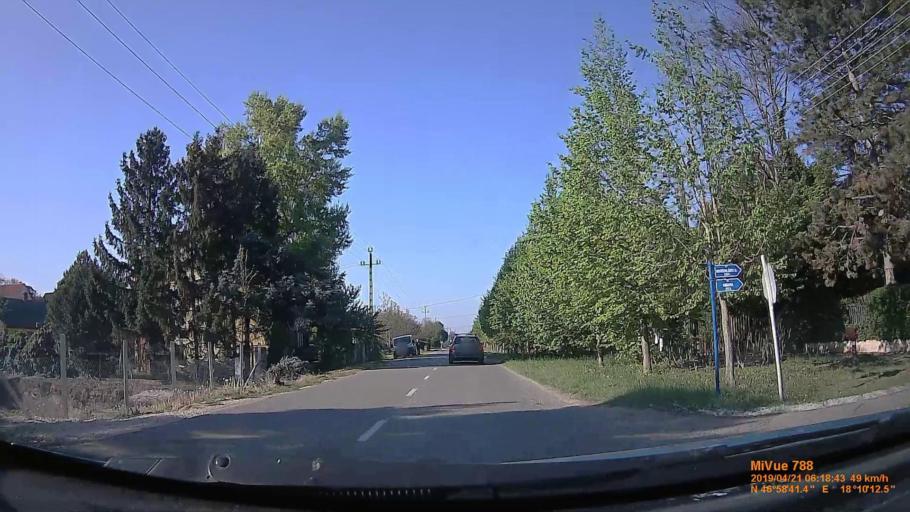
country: HU
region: Fejer
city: Lepseny
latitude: 46.9782
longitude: 18.1701
